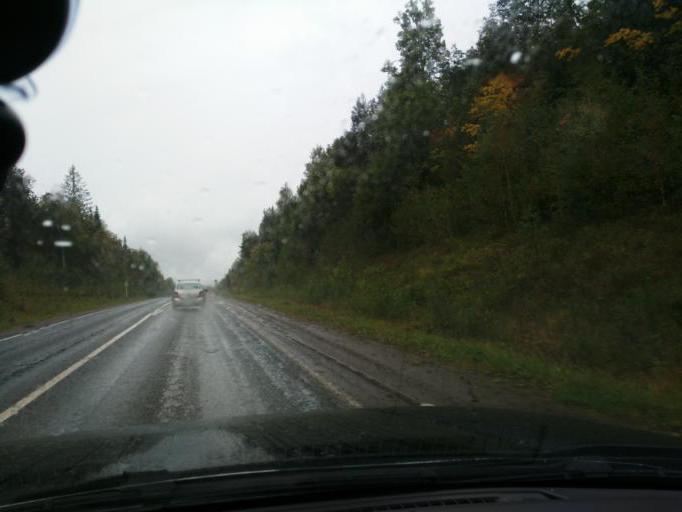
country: RU
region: Perm
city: Yugo-Kamskiy
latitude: 57.6069
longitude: 55.6519
